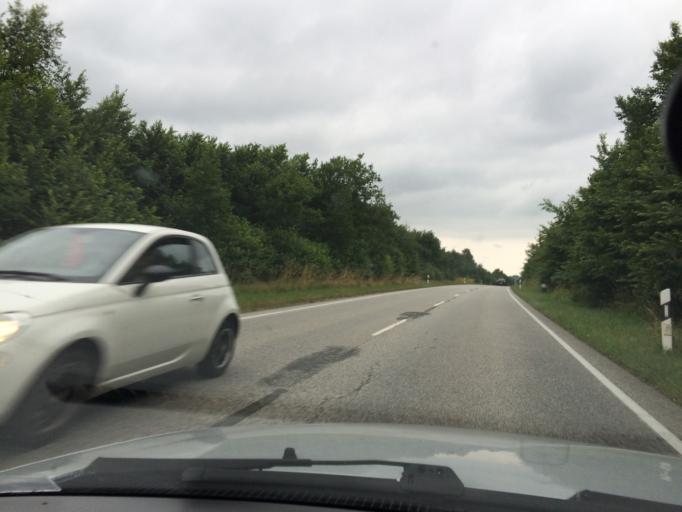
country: DE
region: Schleswig-Holstein
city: Oeversee
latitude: 54.6834
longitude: 9.4338
